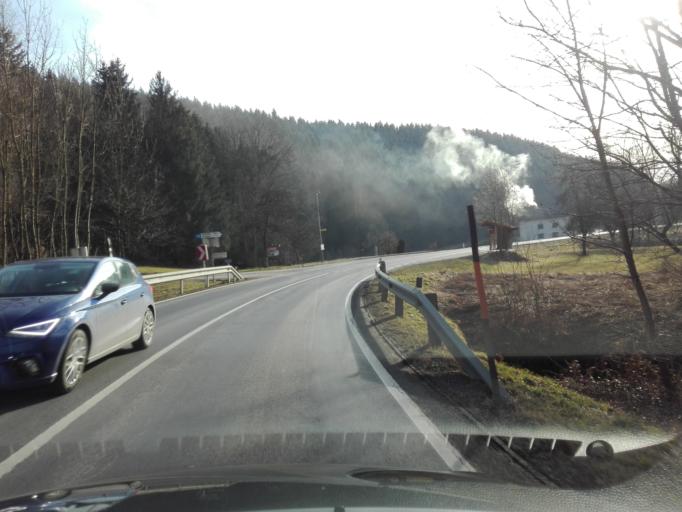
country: AT
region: Lower Austria
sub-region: Politischer Bezirk Amstetten
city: Amstetten
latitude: 48.1902
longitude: 14.8493
